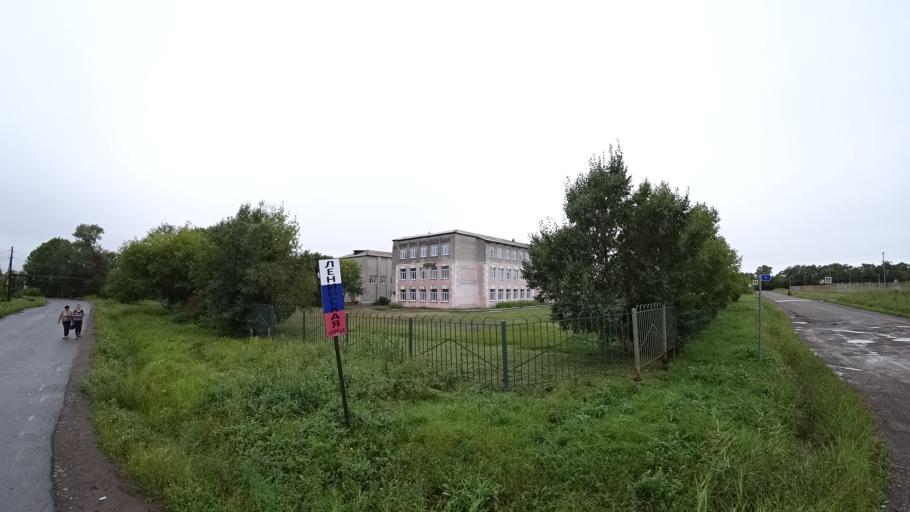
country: RU
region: Primorskiy
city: Monastyrishche
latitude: 44.1957
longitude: 132.4255
